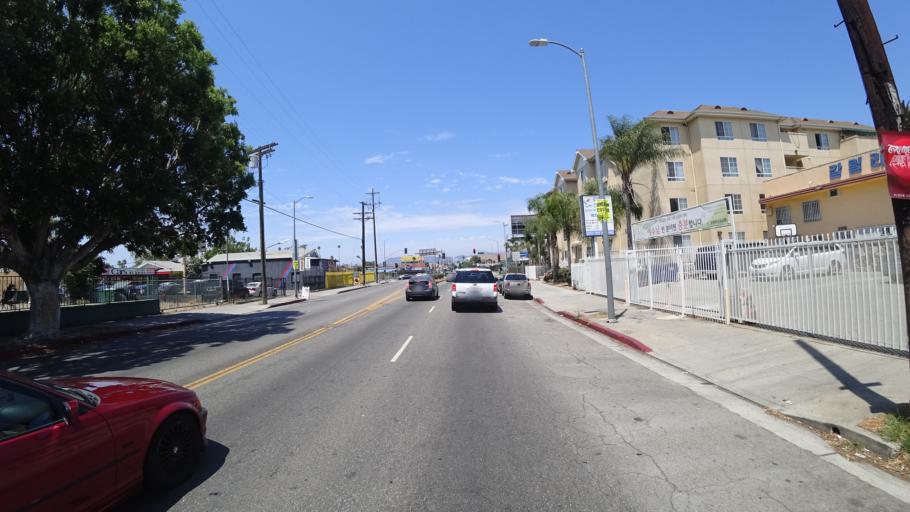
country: US
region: California
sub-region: Los Angeles County
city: View Park-Windsor Hills
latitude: 34.0357
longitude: -118.3089
